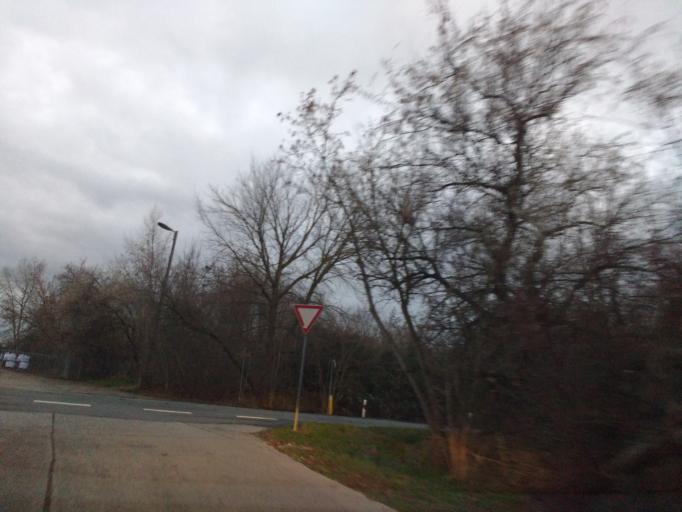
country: DE
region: Saxony-Anhalt
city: Mucheln
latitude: 51.3108
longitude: 11.8018
